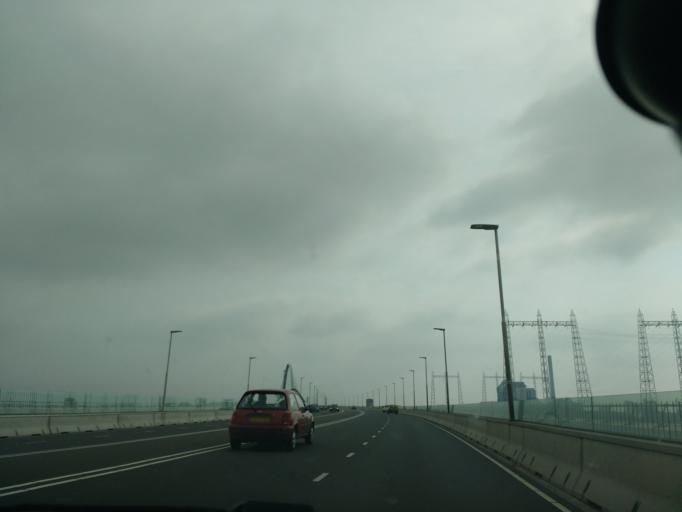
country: NL
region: Gelderland
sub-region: Gemeente Nijmegen
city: Nijmegen
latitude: 51.8641
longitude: 5.8460
